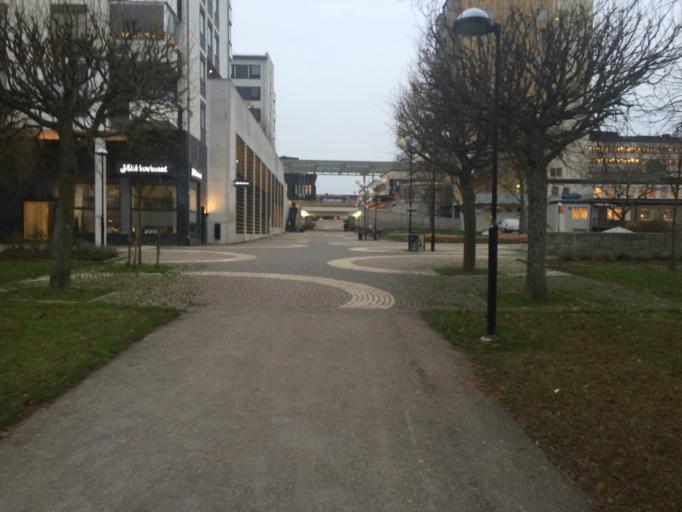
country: SE
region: Stockholm
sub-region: Stockholms Kommun
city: Bromma
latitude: 59.3643
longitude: 17.8754
